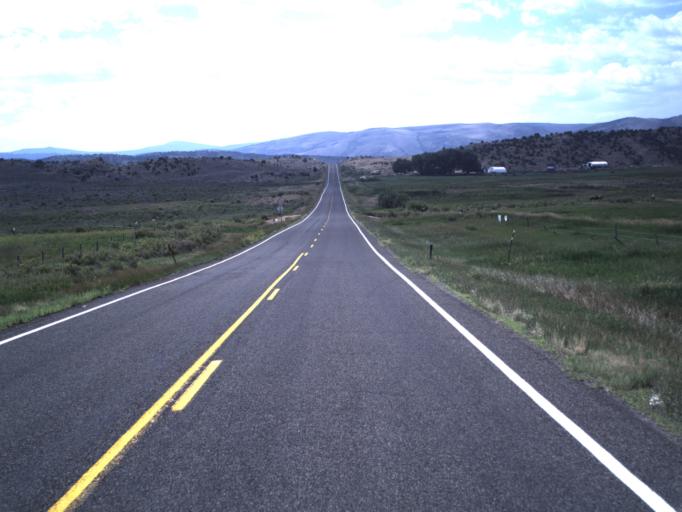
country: US
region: Utah
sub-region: Daggett County
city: Manila
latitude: 40.9662
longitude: -109.7131
